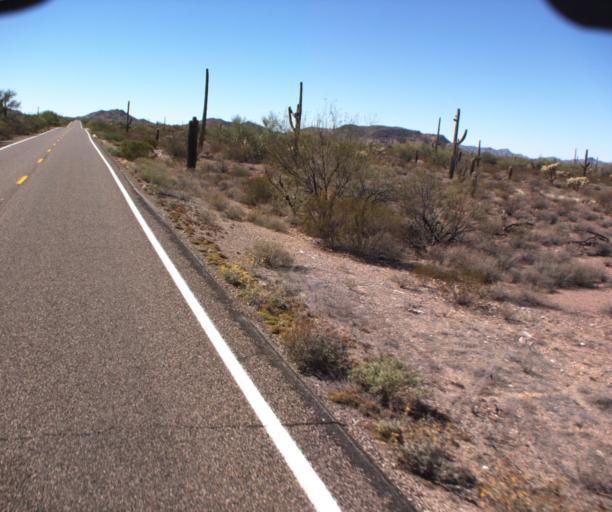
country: MX
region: Sonora
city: Sonoyta
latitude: 32.1140
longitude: -112.7696
